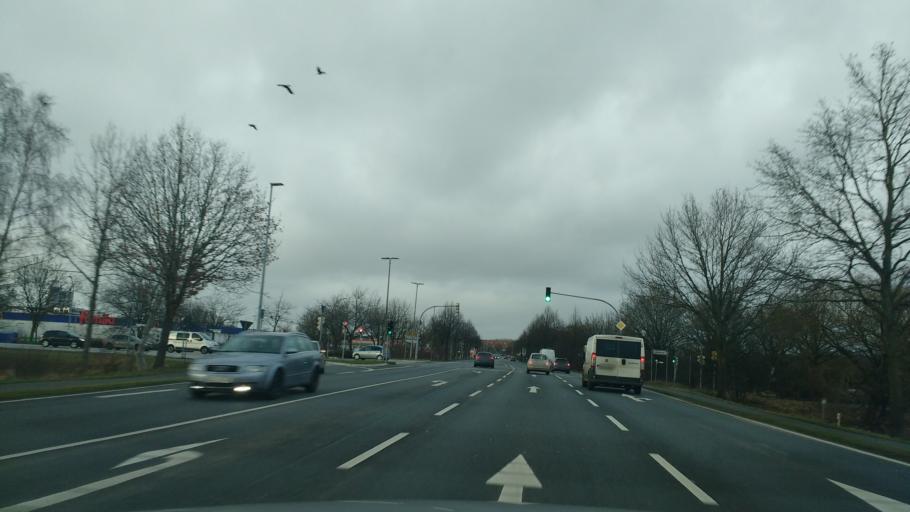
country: DE
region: Schleswig-Holstein
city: Itzehoe
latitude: 53.9126
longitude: 9.5160
